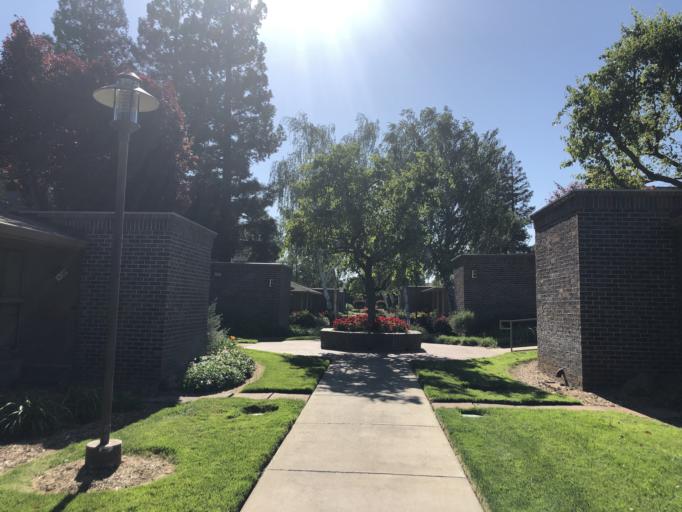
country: US
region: California
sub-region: Santa Clara County
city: Gilroy
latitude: 37.0097
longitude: -121.5855
